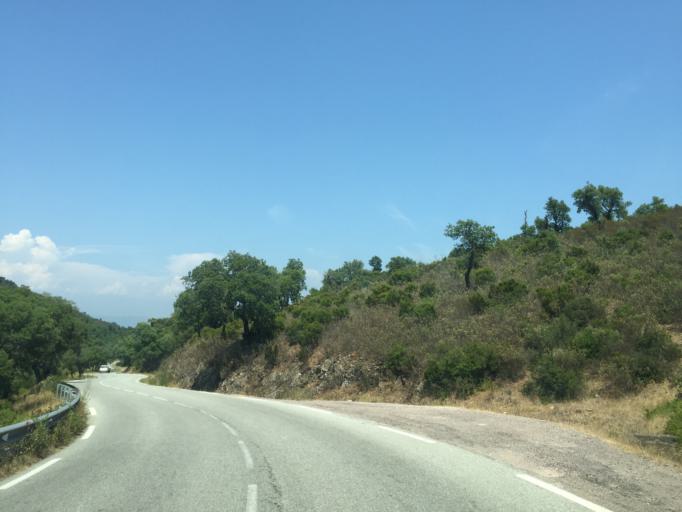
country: FR
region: Provence-Alpes-Cote d'Azur
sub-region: Departement du Var
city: Sainte-Maxime
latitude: 43.3703
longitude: 6.6729
